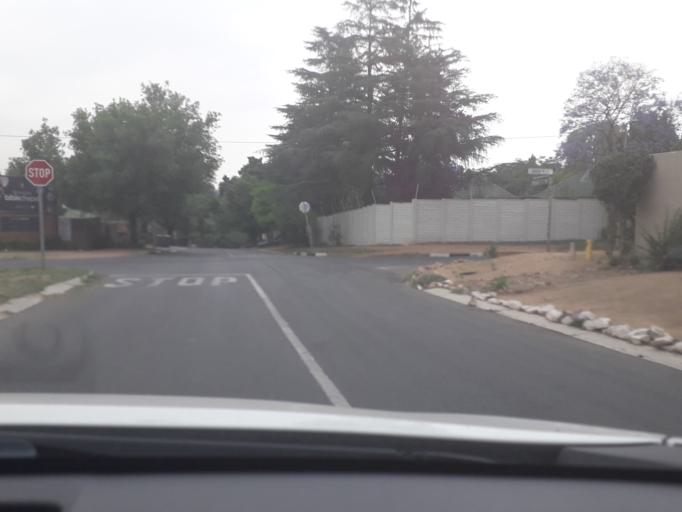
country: ZA
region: Gauteng
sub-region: City of Johannesburg Metropolitan Municipality
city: Johannesburg
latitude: -26.0884
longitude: 27.9937
